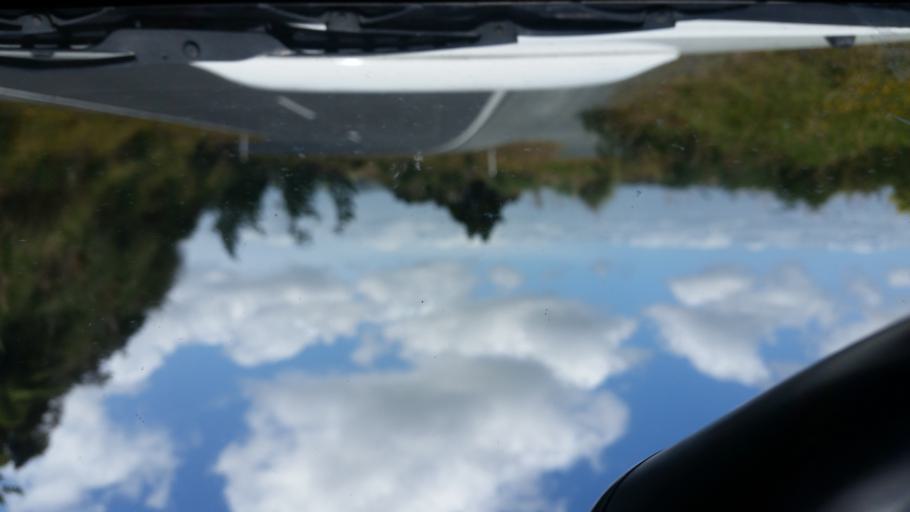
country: NZ
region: Northland
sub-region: Whangarei
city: Ruakaka
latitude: -36.0829
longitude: 174.2393
